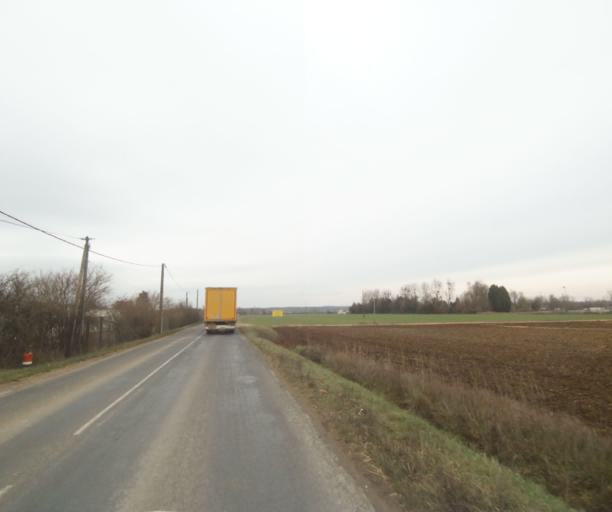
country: FR
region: Champagne-Ardenne
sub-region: Departement de la Haute-Marne
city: Villiers-en-Lieu
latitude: 48.6512
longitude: 4.9068
